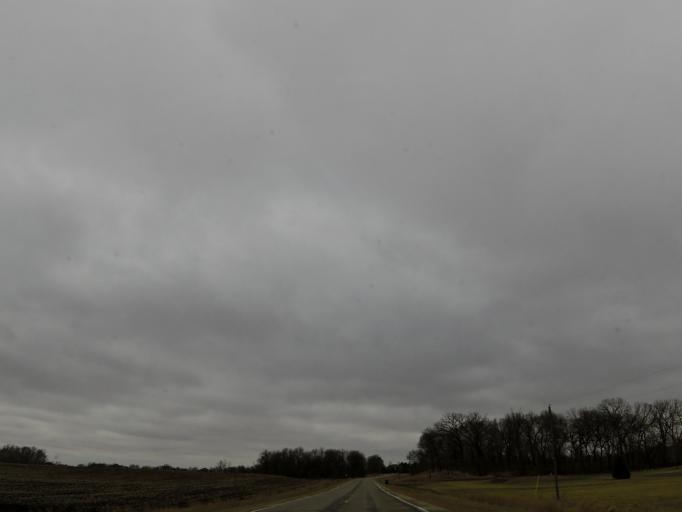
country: US
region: Minnesota
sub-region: Scott County
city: Shakopee
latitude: 44.7272
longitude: -93.5208
